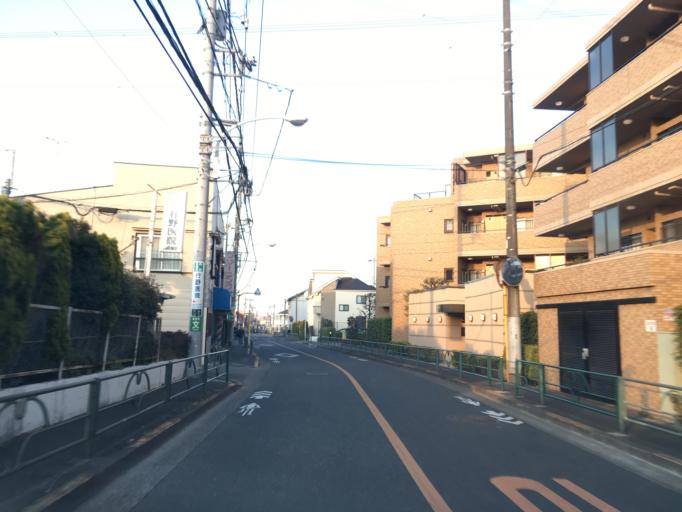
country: JP
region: Tokyo
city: Kokubunji
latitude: 35.7049
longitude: 139.4550
